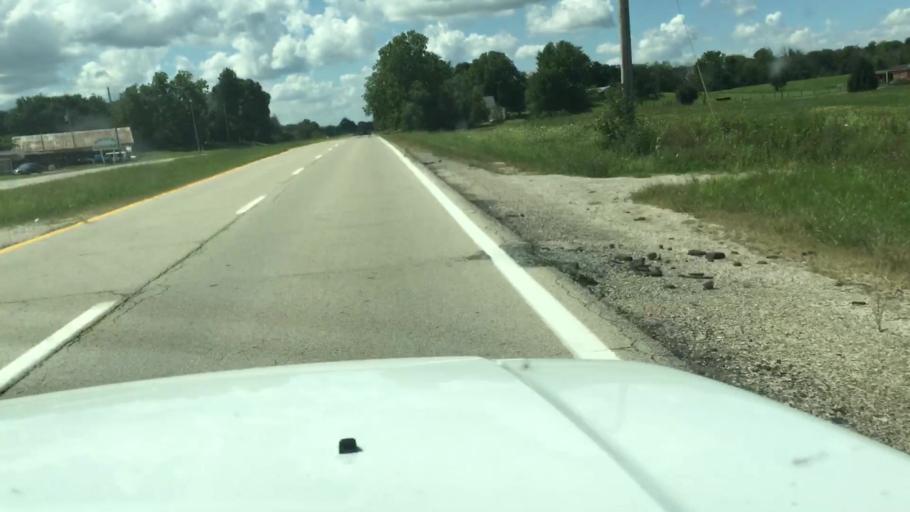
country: US
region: Ohio
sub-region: Madison County
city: Choctaw Lake
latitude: 39.9318
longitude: -83.5343
